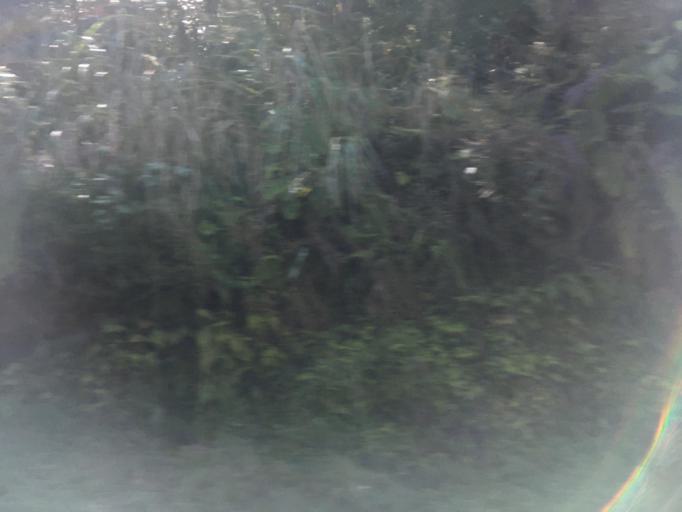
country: TW
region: Taiwan
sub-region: Yilan
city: Yilan
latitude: 24.5234
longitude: 121.5182
